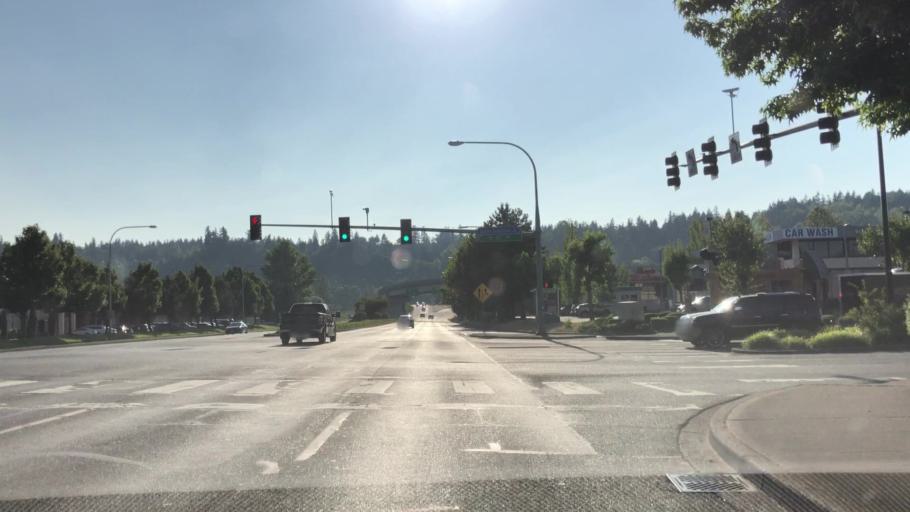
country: US
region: Washington
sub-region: King County
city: Algona
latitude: 47.2958
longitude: -122.2496
